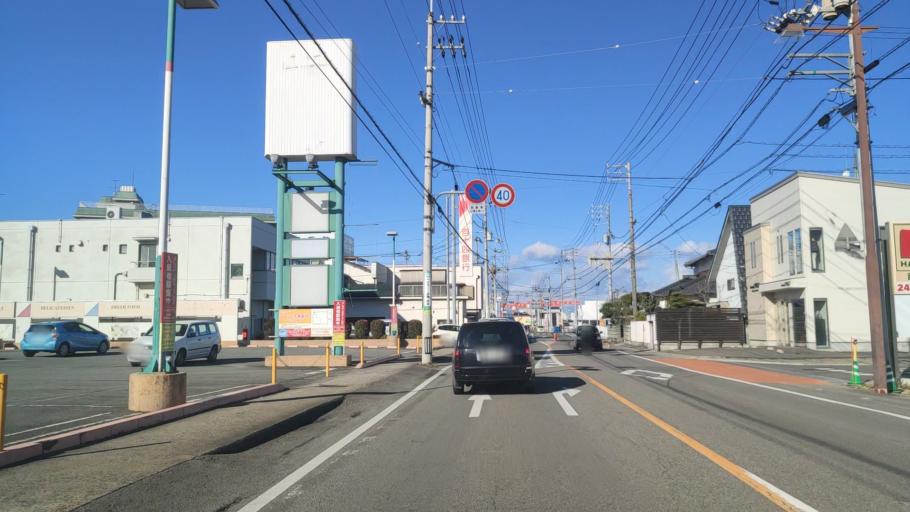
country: JP
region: Ehime
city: Saijo
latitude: 33.9192
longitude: 133.1918
